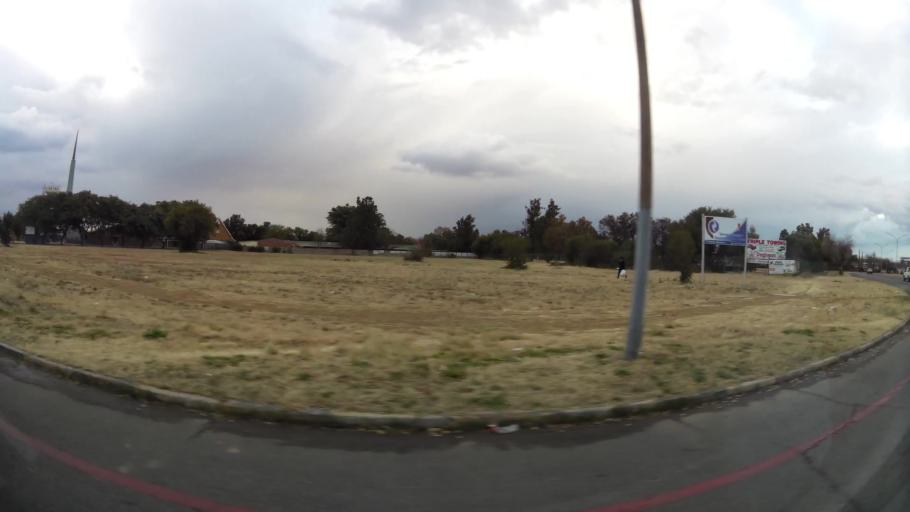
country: ZA
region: Orange Free State
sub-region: Lejweleputswa District Municipality
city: Welkom
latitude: -27.9639
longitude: 26.7395
